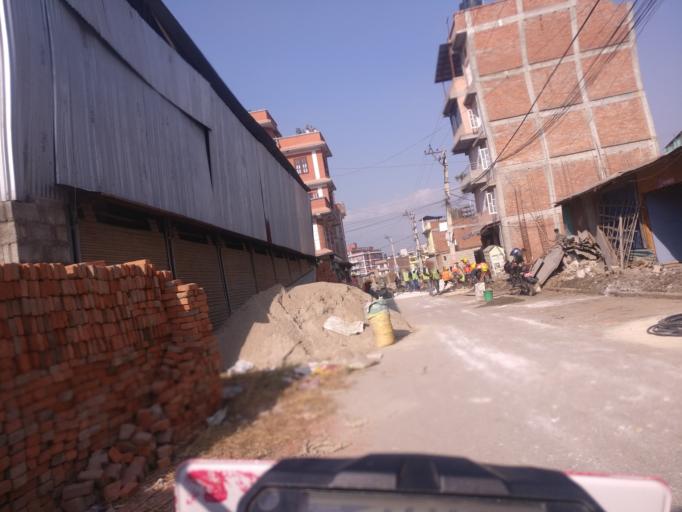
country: NP
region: Central Region
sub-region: Bagmati Zone
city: Patan
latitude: 27.6814
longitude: 85.3284
